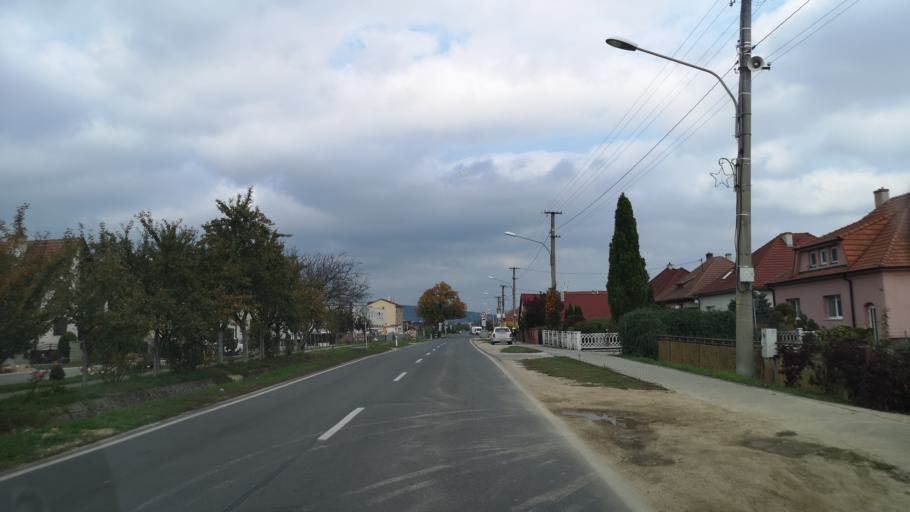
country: SK
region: Nitriansky
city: Cachtice
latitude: 48.6880
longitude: 17.7799
